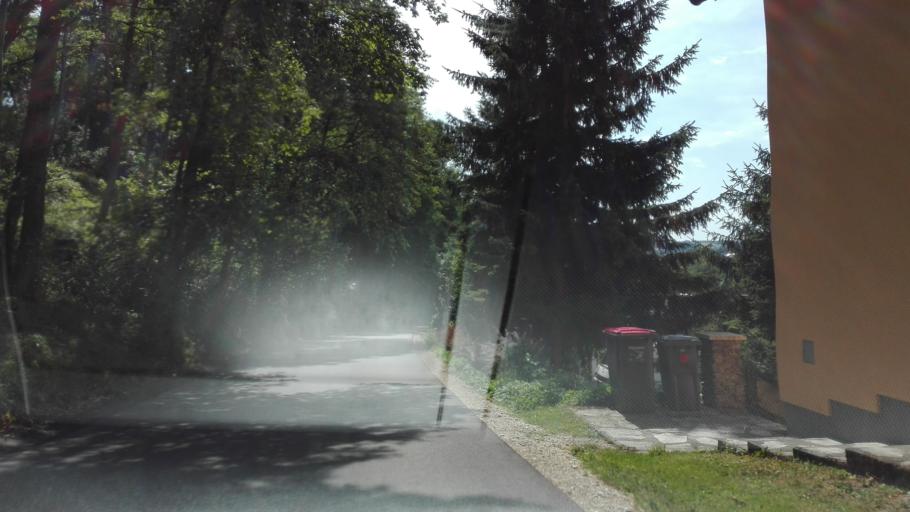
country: AT
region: Upper Austria
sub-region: Politischer Bezirk Grieskirchen
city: Bad Schallerbach
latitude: 48.2295
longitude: 13.9531
